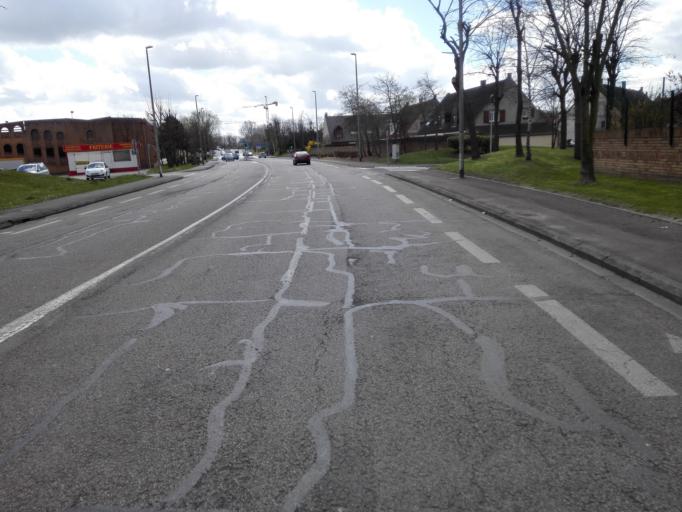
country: FR
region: Nord-Pas-de-Calais
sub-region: Departement du Nord
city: Saint-Pol-sur-Mer
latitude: 51.0262
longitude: 2.3342
